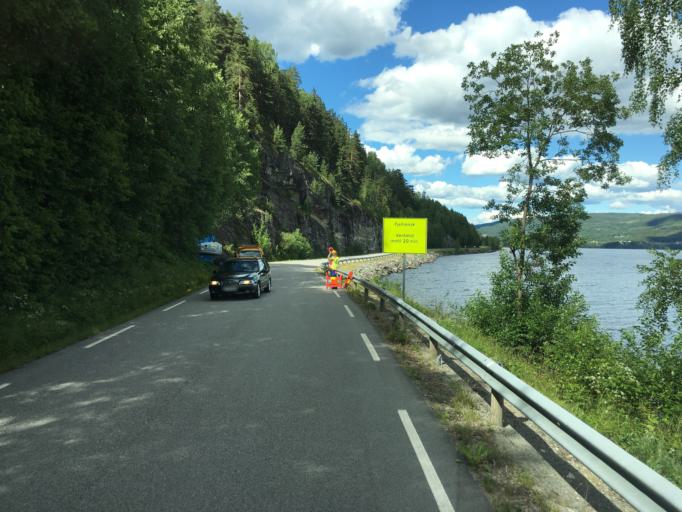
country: NO
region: Oppland
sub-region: Sondre Land
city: Hov
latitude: 60.6010
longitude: 10.3229
